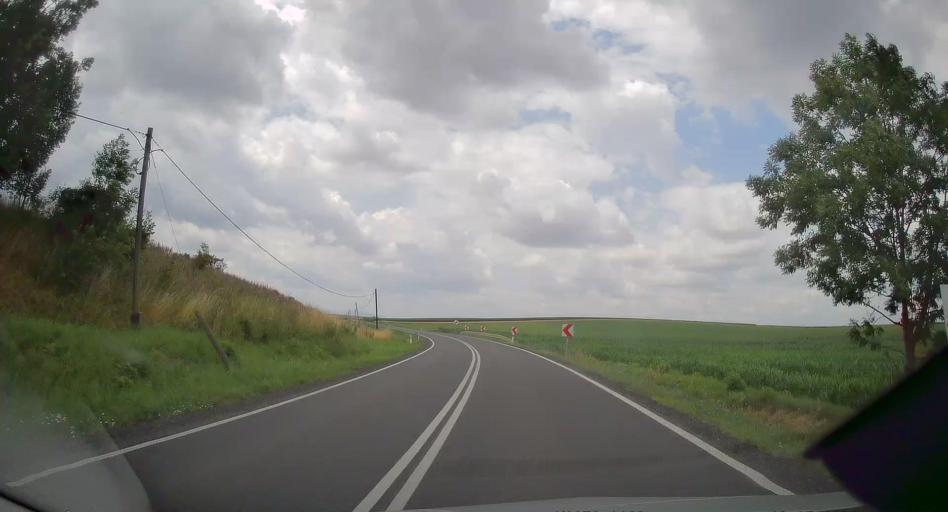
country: PL
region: Opole Voivodeship
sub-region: Powiat prudnicki
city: Glogowek
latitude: 50.3548
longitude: 17.8262
